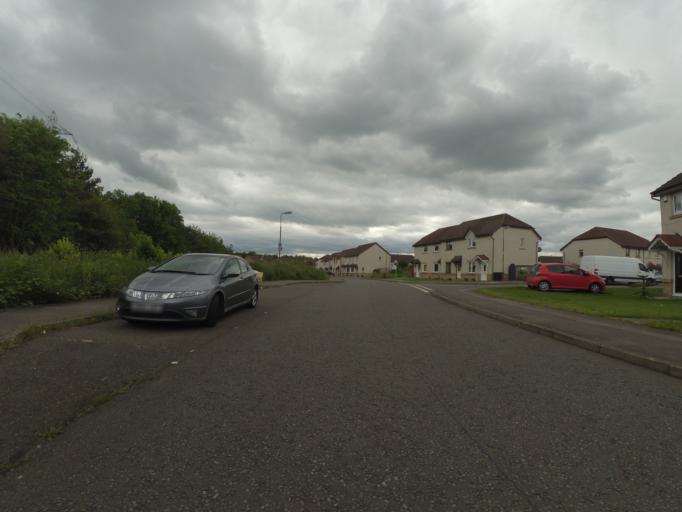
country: GB
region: Scotland
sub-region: East Lothian
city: Musselburgh
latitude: 55.9382
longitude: -3.0962
